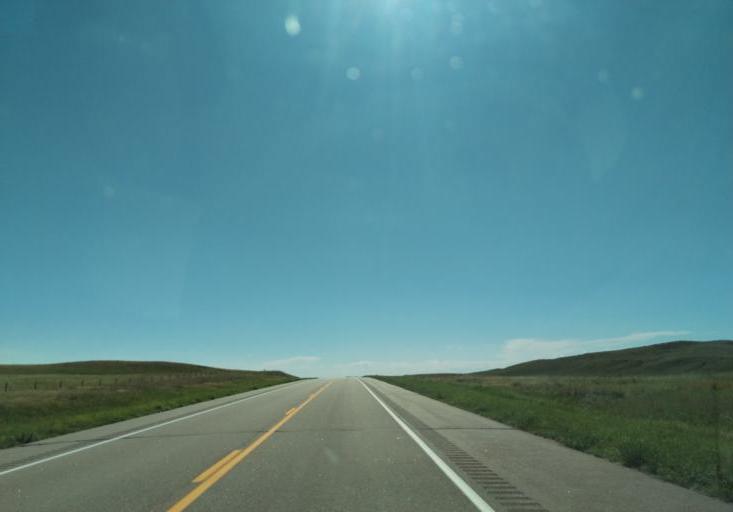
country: US
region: South Dakota
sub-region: Bennett County
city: Martin
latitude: 42.9392
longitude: -101.3584
